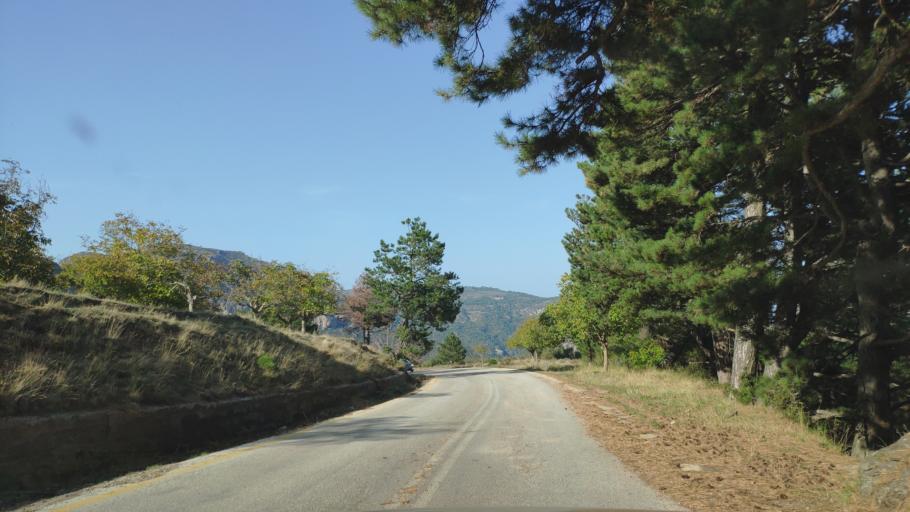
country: GR
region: West Greece
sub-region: Nomos Achaias
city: Aiyira
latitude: 38.0570
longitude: 22.3816
